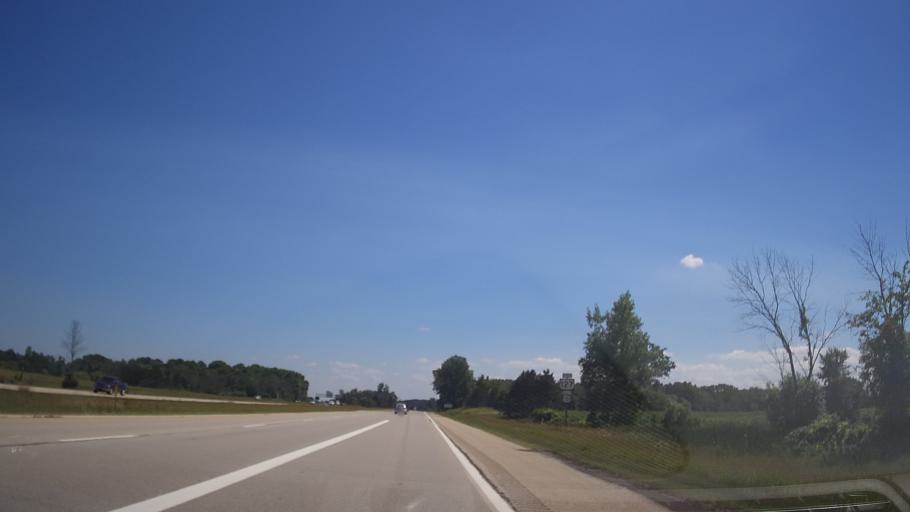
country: US
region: Michigan
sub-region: Clare County
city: Clare
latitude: 43.8713
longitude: -84.7789
